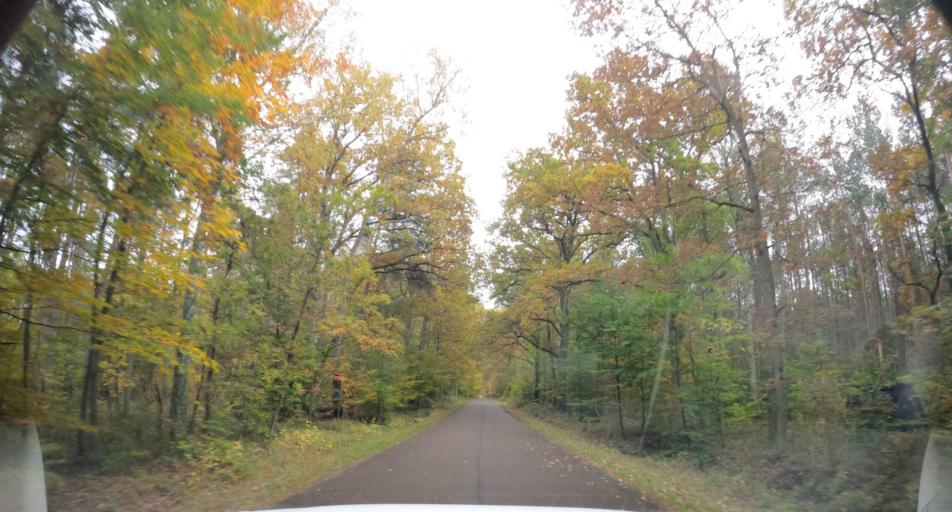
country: PL
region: West Pomeranian Voivodeship
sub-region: Powiat kamienski
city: Wolin
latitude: 53.9156
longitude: 14.5622
